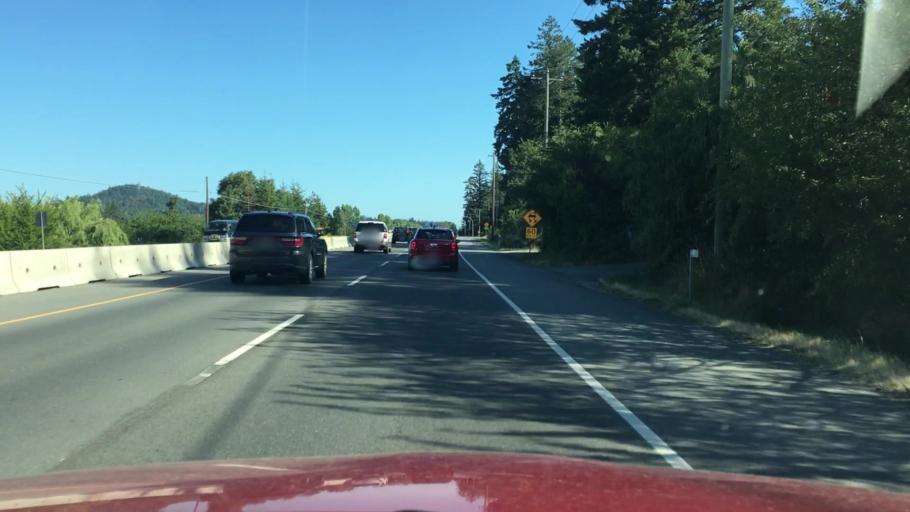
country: CA
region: British Columbia
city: Victoria
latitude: 48.5194
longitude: -123.3853
